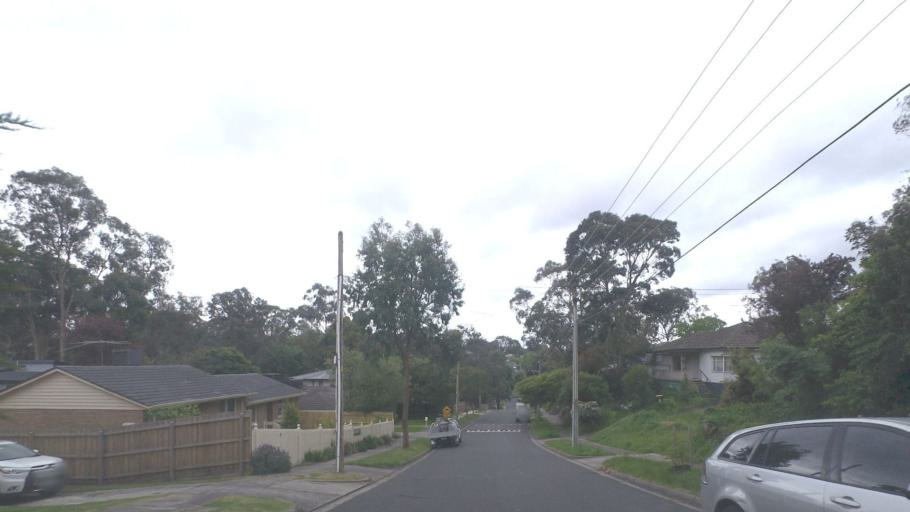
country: AU
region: Victoria
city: Mitcham
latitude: -37.8118
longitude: 145.1992
